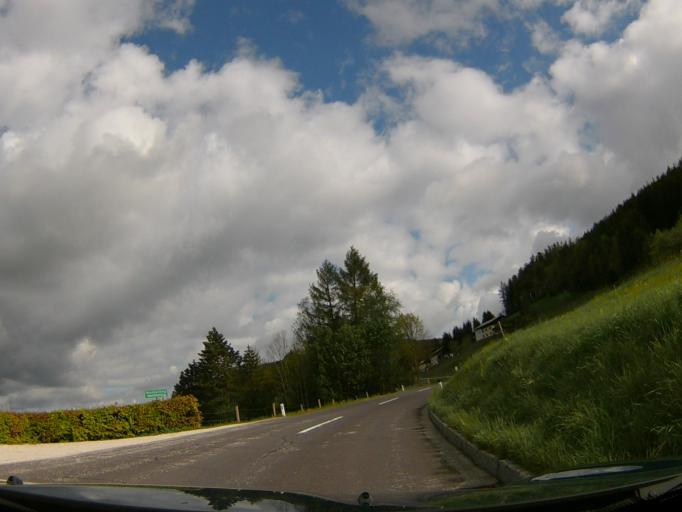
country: AT
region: Upper Austria
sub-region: Politischer Bezirk Vocklabruck
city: Mondsee
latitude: 47.8677
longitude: 13.3522
